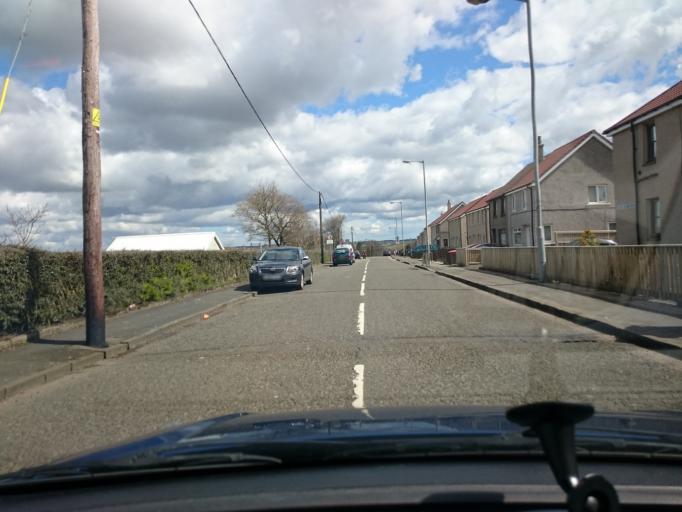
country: GB
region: Scotland
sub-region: Falkirk
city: Slamannan
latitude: 55.9354
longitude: -3.8407
